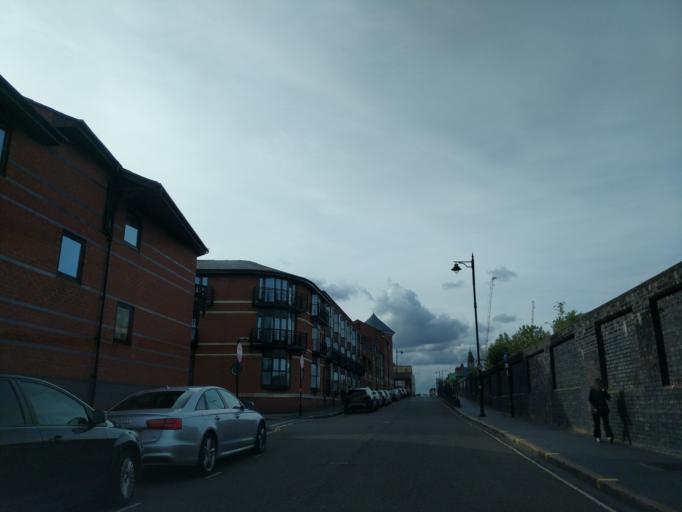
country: GB
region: England
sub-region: City and Borough of Birmingham
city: Birmingham
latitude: 52.4866
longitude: -1.9044
